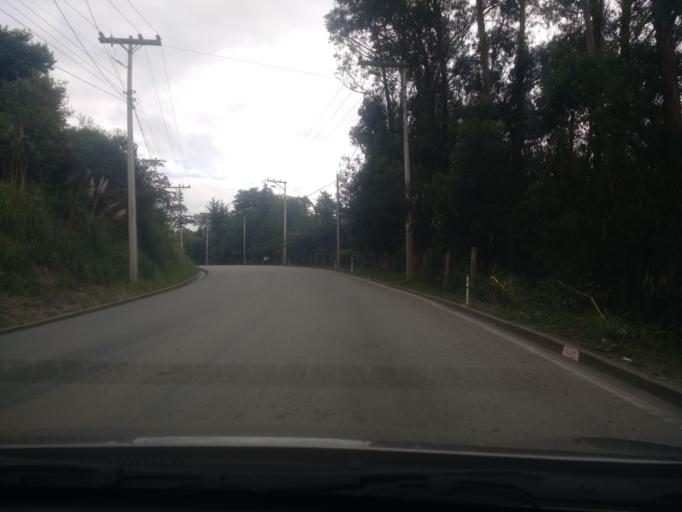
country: EC
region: Azuay
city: La Union
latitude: -2.8437
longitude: -78.7729
